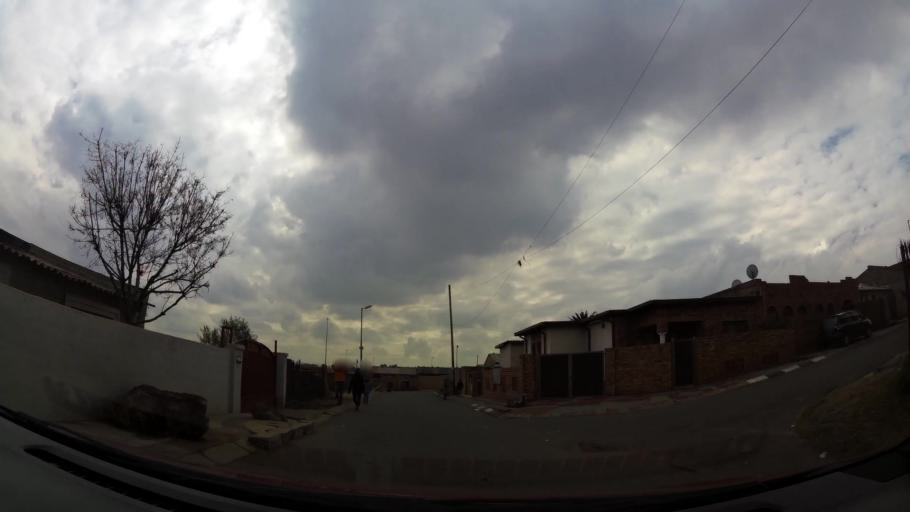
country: ZA
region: Gauteng
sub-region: City of Johannesburg Metropolitan Municipality
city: Soweto
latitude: -26.2538
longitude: 27.8237
